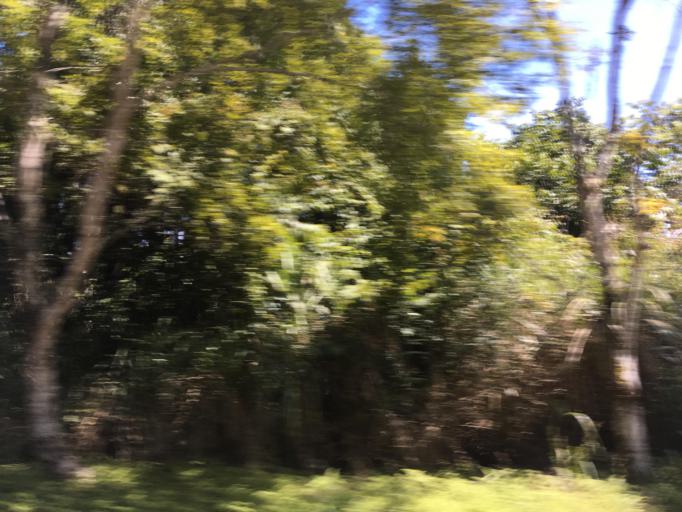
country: TW
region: Taiwan
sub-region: Yilan
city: Yilan
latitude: 24.5224
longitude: 121.5212
